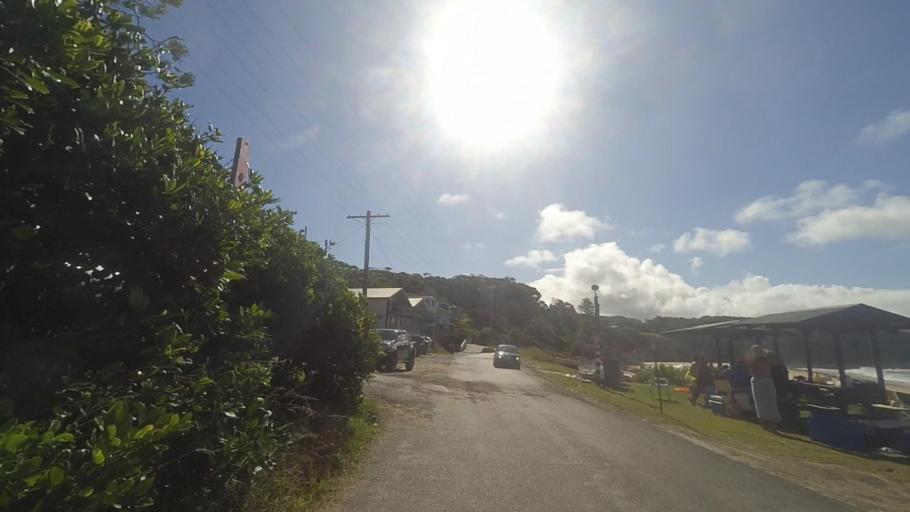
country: AU
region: New South Wales
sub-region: Great Lakes
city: Forster
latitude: -32.4358
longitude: 152.5324
